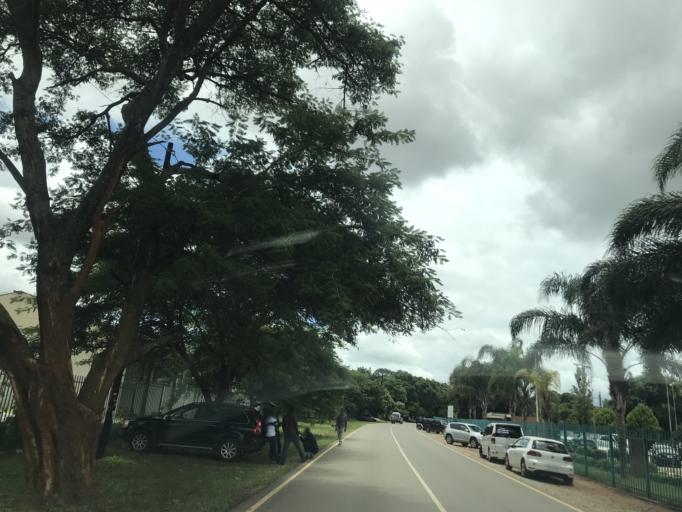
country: ZM
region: Lusaka
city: Lusaka
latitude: -15.4293
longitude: 28.3087
